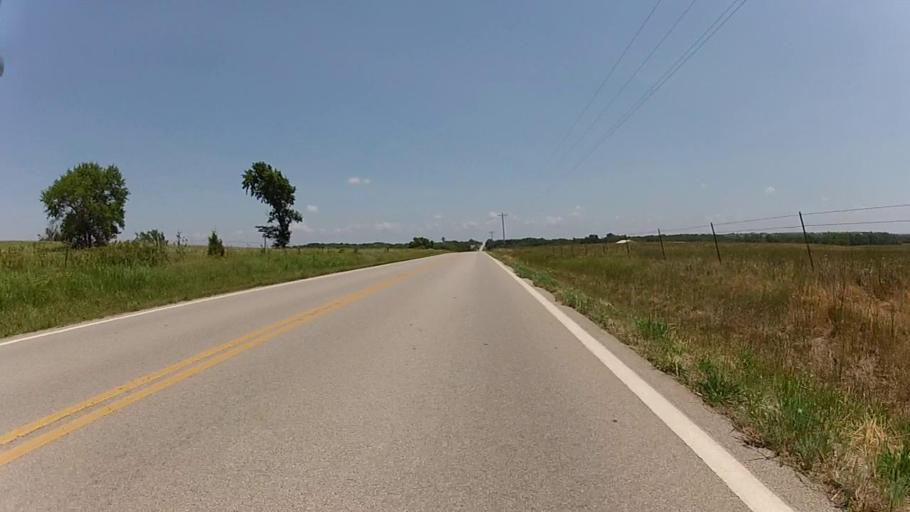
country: US
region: Kansas
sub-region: Montgomery County
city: Cherryvale
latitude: 37.1937
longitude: -95.5199
